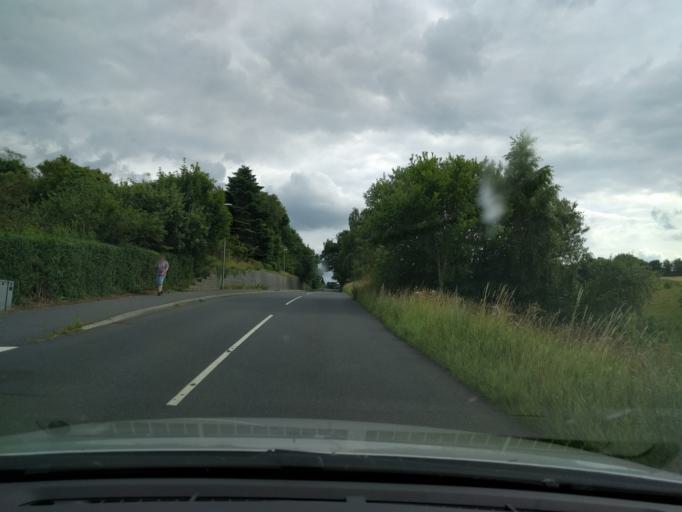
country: DK
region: Central Jutland
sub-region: Skanderborg Kommune
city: Ry
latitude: 56.2142
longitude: 9.7439
